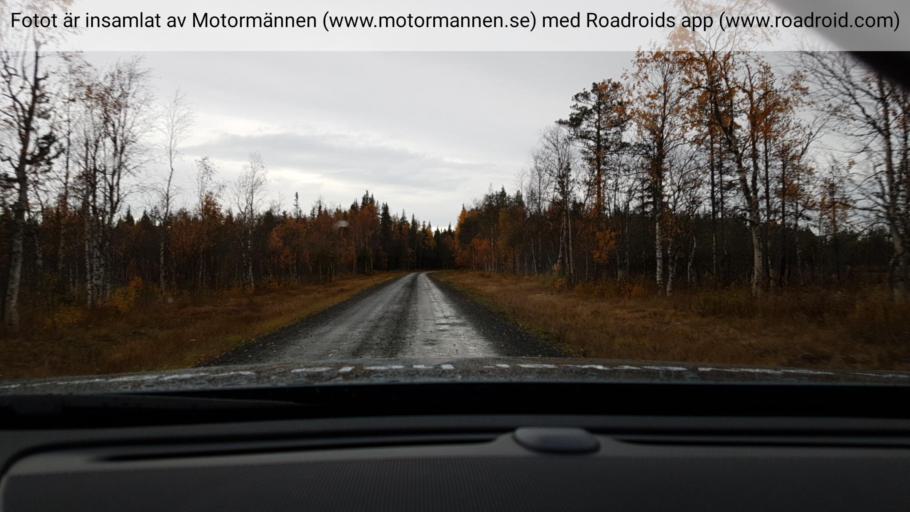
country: SE
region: Norrbotten
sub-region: Pajala Kommun
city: Pajala
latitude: 67.0913
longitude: 22.7487
